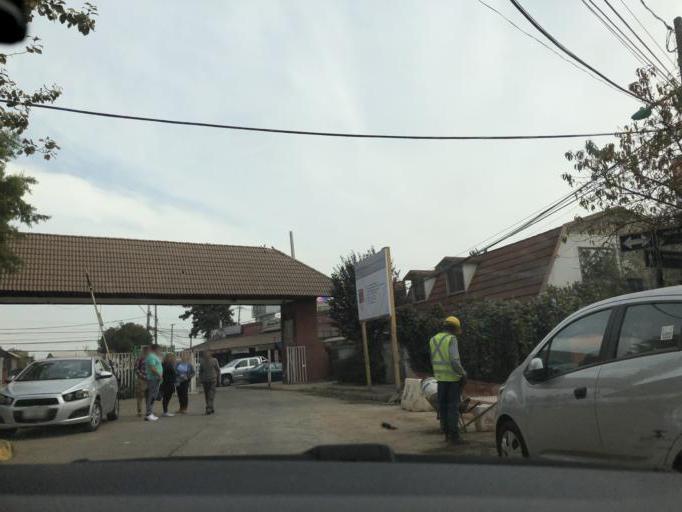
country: CL
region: Santiago Metropolitan
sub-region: Provincia de Cordillera
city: Puente Alto
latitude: -33.5571
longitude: -70.5592
